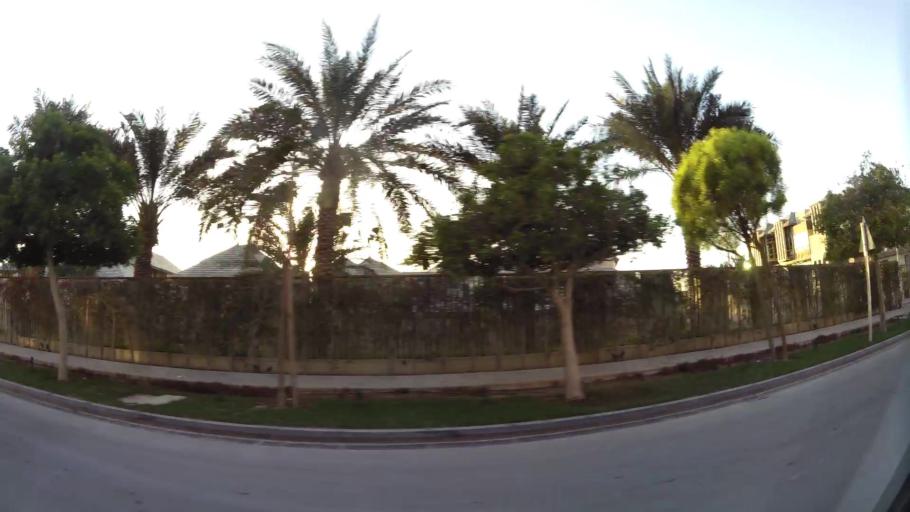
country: BH
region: Manama
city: Jidd Hafs
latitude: 26.2429
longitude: 50.5673
